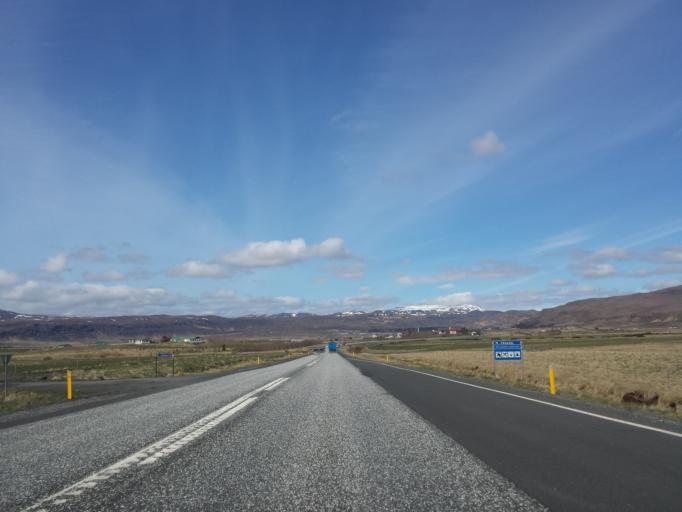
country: IS
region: South
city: Hveragerdi
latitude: 63.9625
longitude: -21.1275
